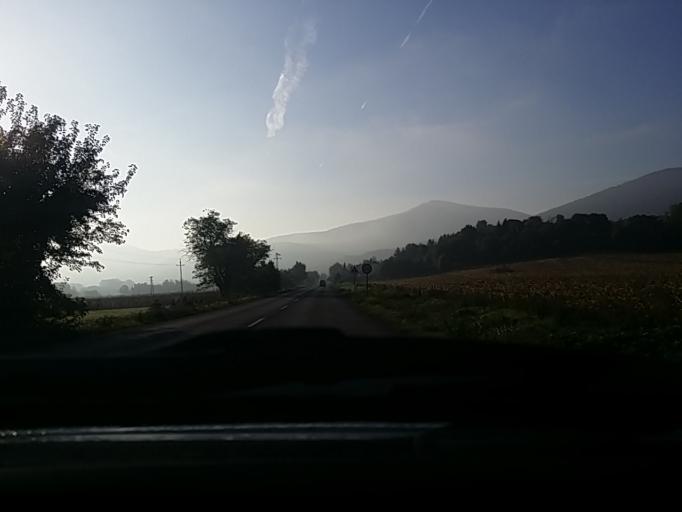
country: HU
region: Komarom-Esztergom
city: Pilismarot
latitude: 47.7745
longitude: 18.8972
